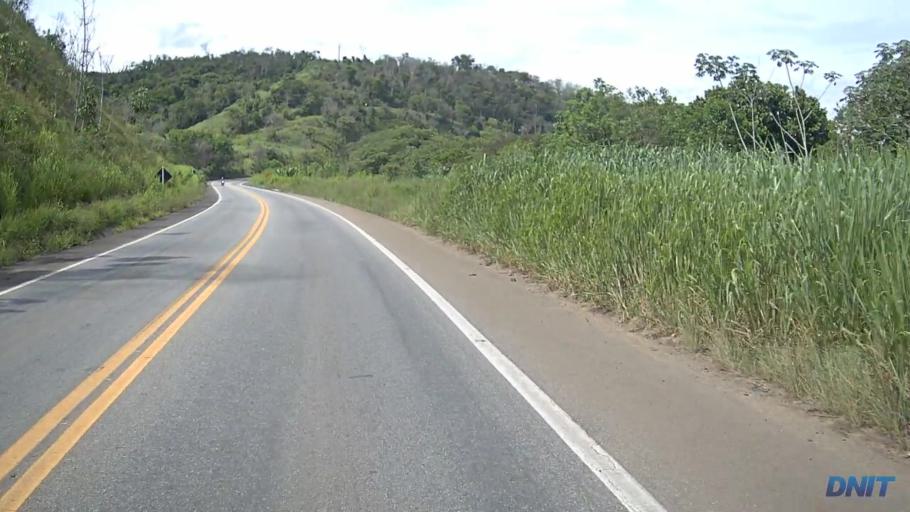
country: BR
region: Minas Gerais
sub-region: Ipaba
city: Ipaba
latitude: -19.3879
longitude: -42.4761
